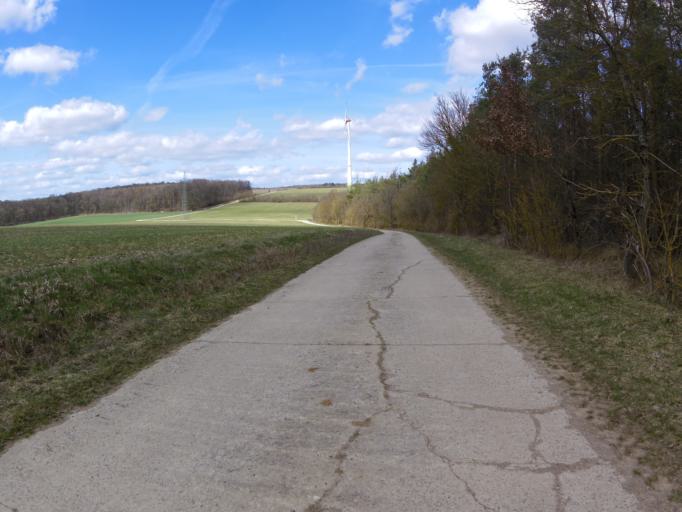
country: DE
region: Bavaria
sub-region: Regierungsbezirk Unterfranken
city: Hettstadt
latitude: 49.8190
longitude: 9.8287
